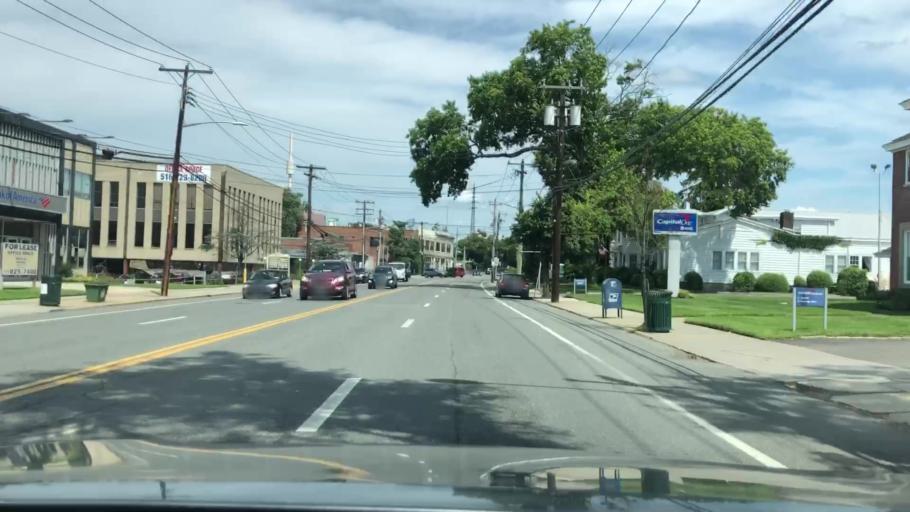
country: US
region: New York
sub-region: Nassau County
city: Baldwin
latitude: 40.6545
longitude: -73.6105
